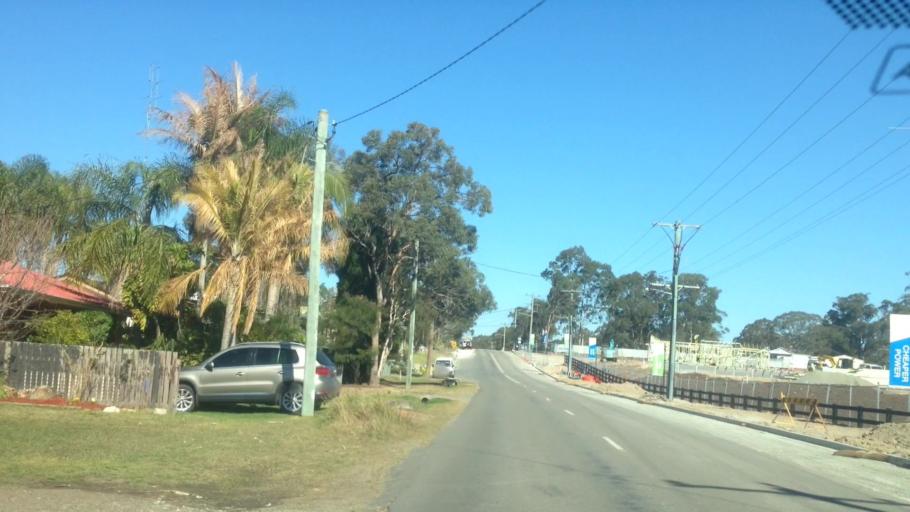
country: AU
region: New South Wales
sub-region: Lake Macquarie Shire
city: Cooranbong
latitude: -33.0911
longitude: 151.4504
